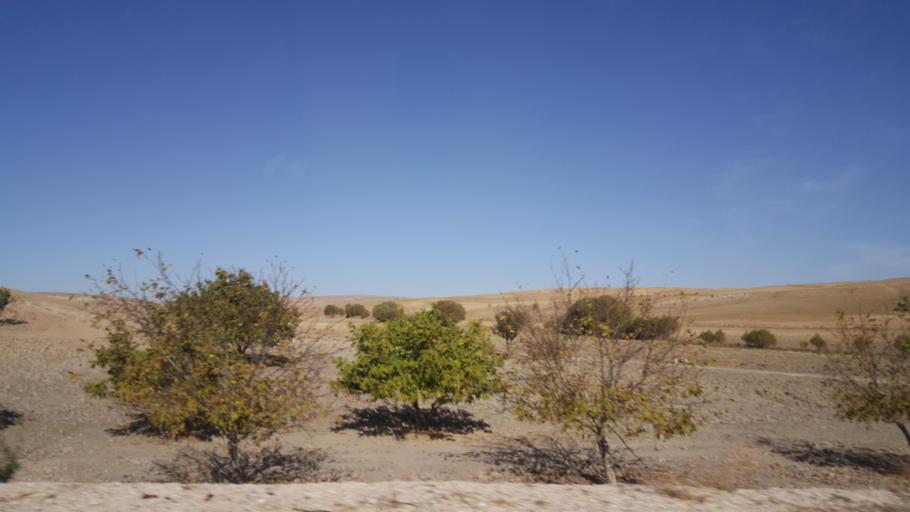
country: TR
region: Ankara
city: Haymana
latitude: 39.4199
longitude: 32.5946
